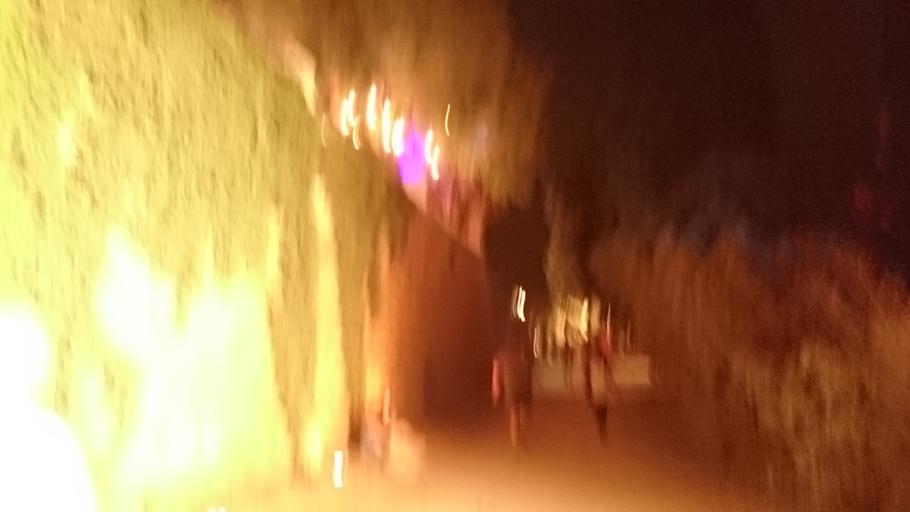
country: ES
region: Catalonia
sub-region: Provincia de Barcelona
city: Vilanova i la Geltru
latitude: 41.2404
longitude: 1.7155
